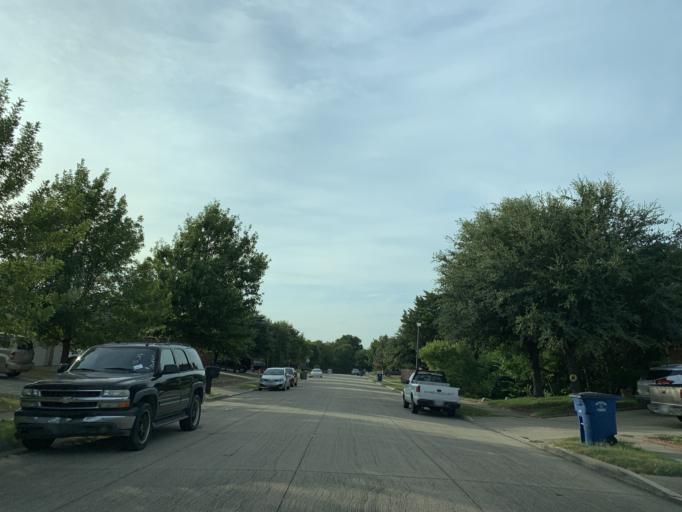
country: US
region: Texas
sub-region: Dallas County
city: Cockrell Hill
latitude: 32.6988
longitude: -96.8953
